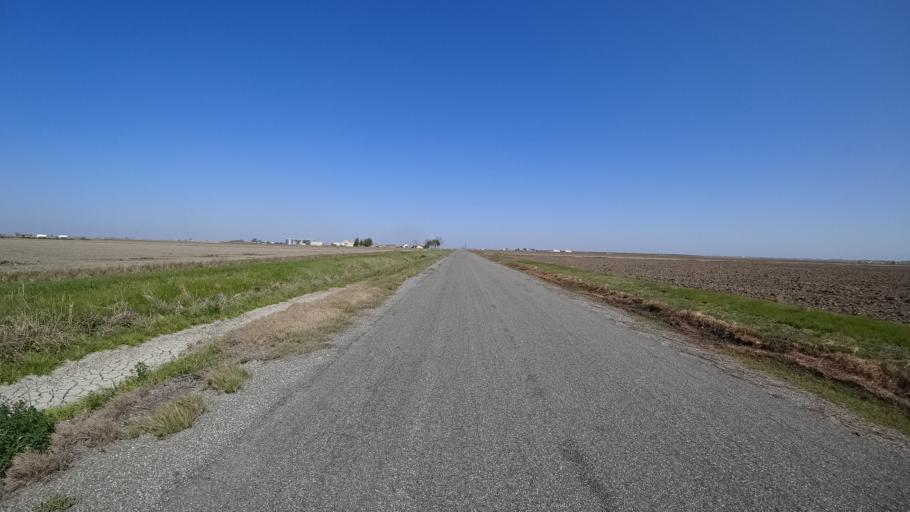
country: US
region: California
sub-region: Glenn County
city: Willows
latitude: 39.5024
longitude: -122.0653
